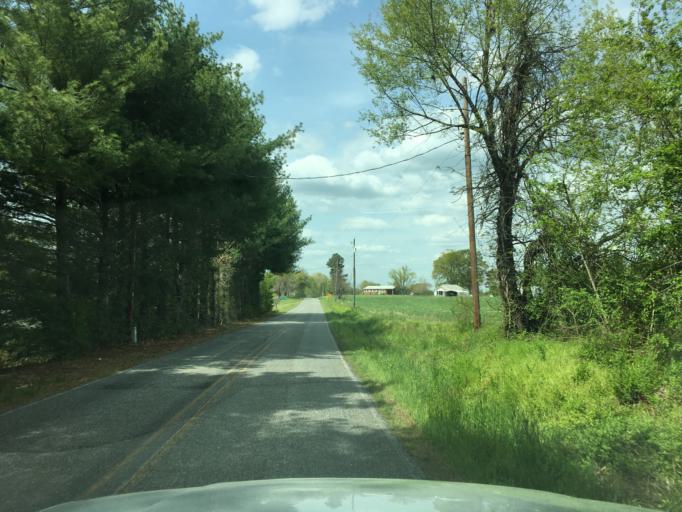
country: US
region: South Carolina
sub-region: Spartanburg County
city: Boiling Springs
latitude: 35.2007
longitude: -81.9707
